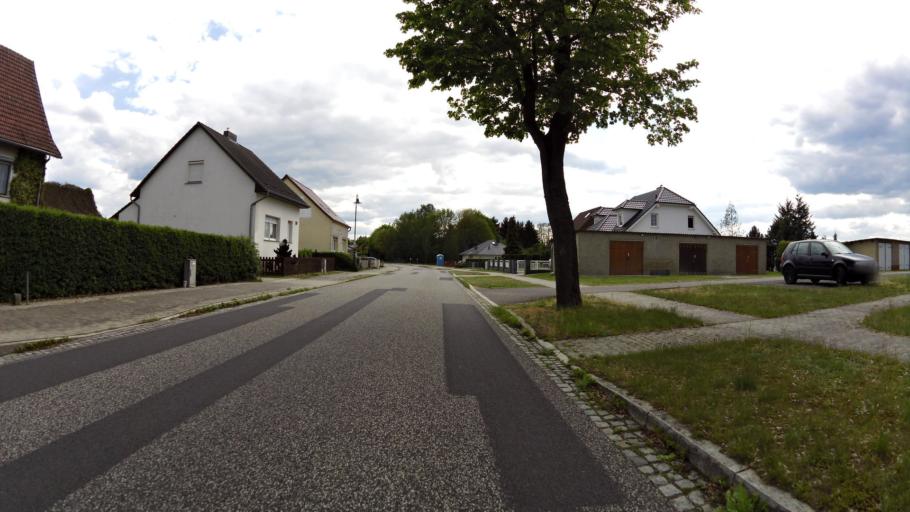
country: DE
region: Brandenburg
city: Rauen
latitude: 52.3337
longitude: 13.9526
